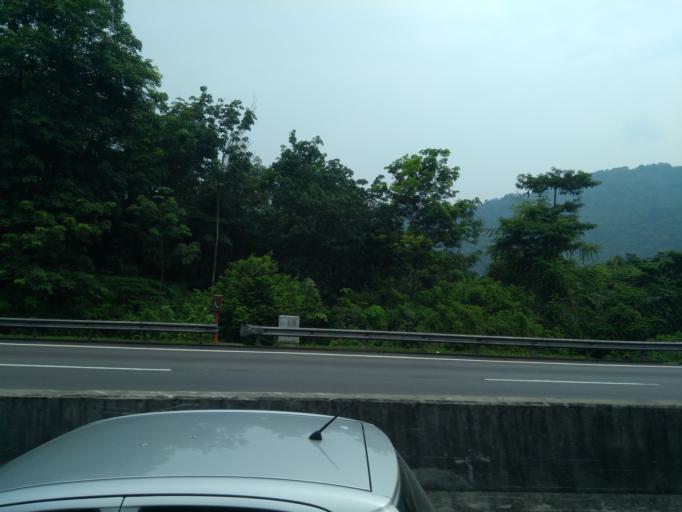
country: MY
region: Perak
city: Ipoh
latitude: 4.6692
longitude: 101.0673
